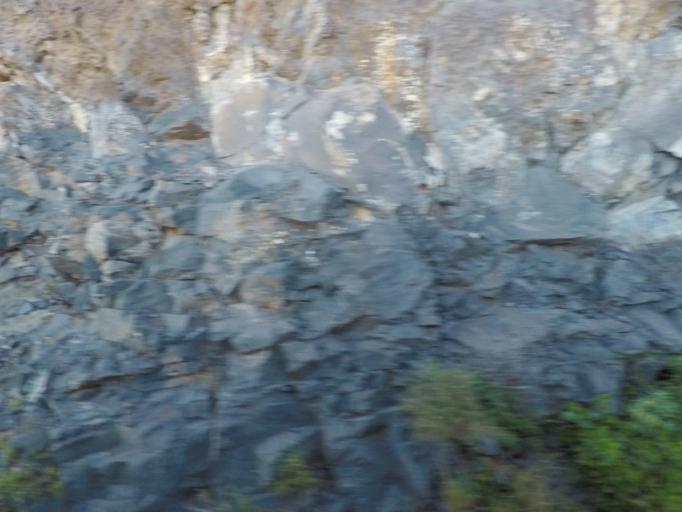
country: ES
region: Canary Islands
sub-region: Provincia de Santa Cruz de Tenerife
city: Alajero
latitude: 28.0554
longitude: -17.2010
